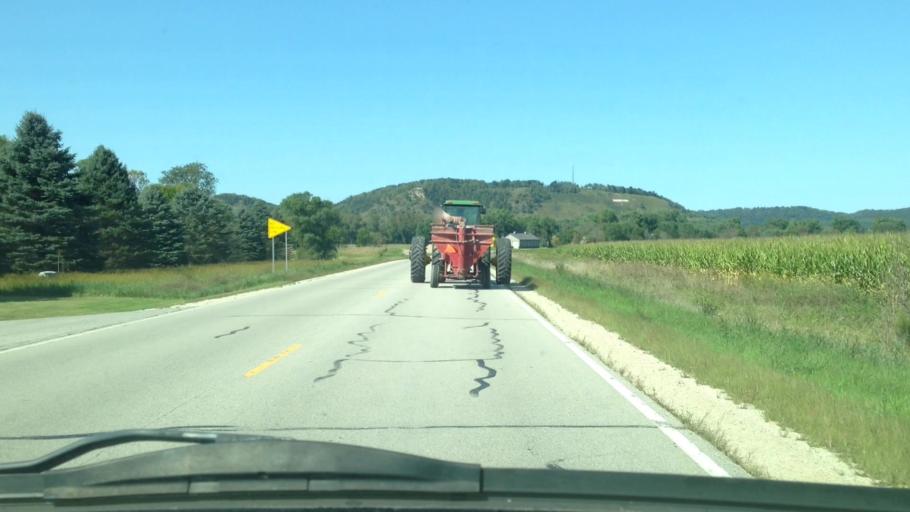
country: US
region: Minnesota
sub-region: Fillmore County
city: Rushford
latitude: 43.7893
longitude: -91.7653
